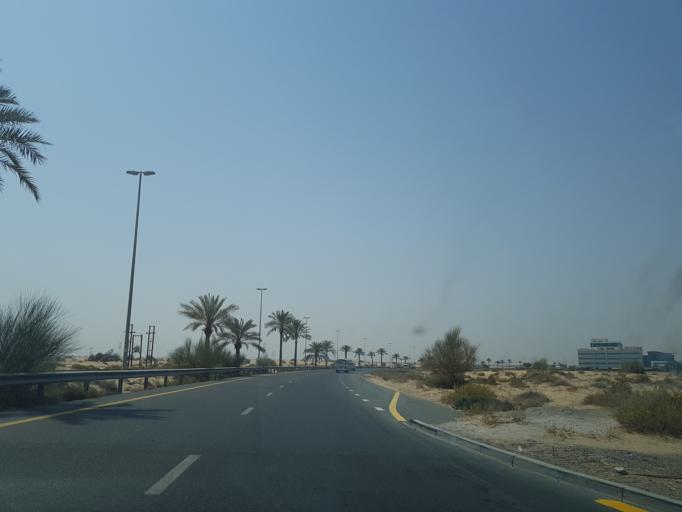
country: AE
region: Ash Shariqah
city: Sharjah
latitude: 25.1329
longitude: 55.4309
